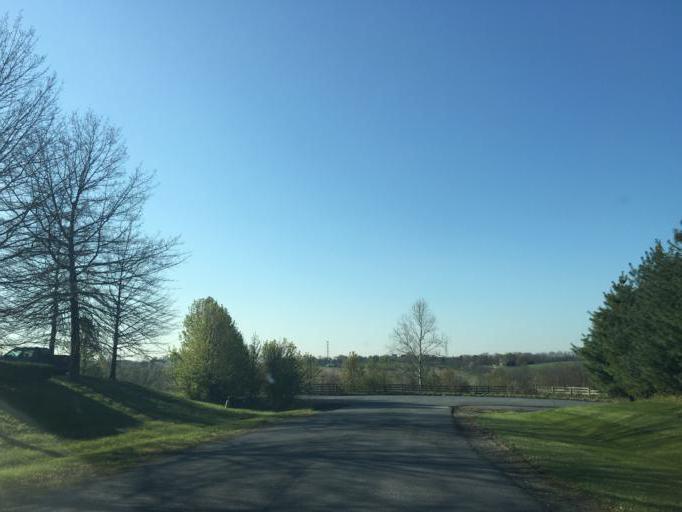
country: US
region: Maryland
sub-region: Frederick County
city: Myersville
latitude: 39.4913
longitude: -77.5654
